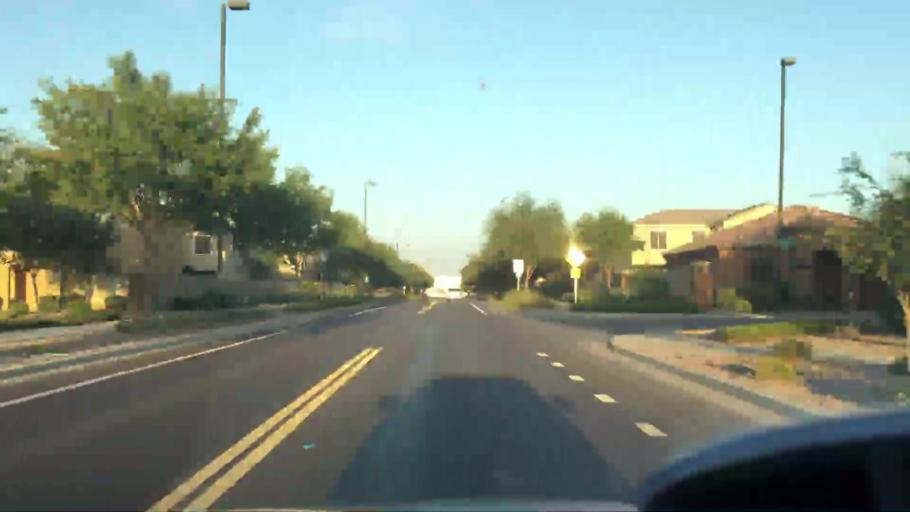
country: US
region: Arizona
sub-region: Maricopa County
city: Gilbert
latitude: 33.3142
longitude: -111.7174
